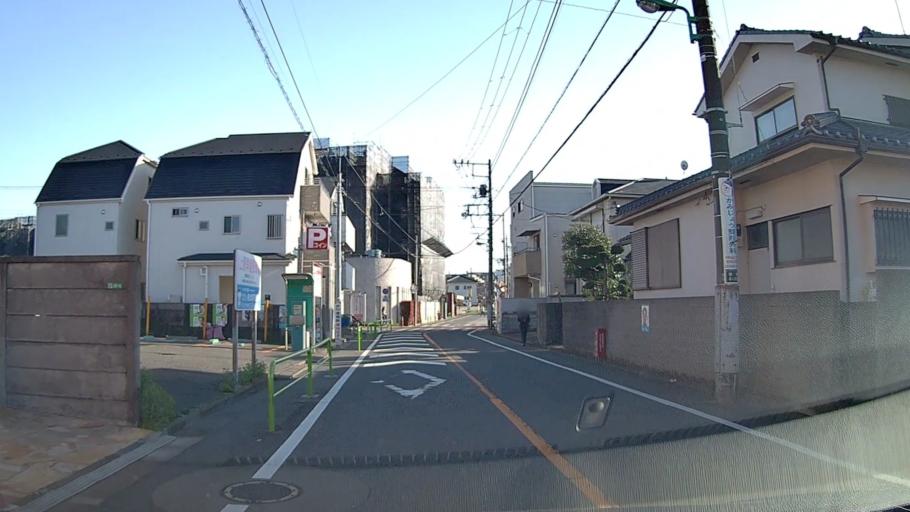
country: JP
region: Saitama
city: Wako
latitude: 35.7532
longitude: 139.6499
